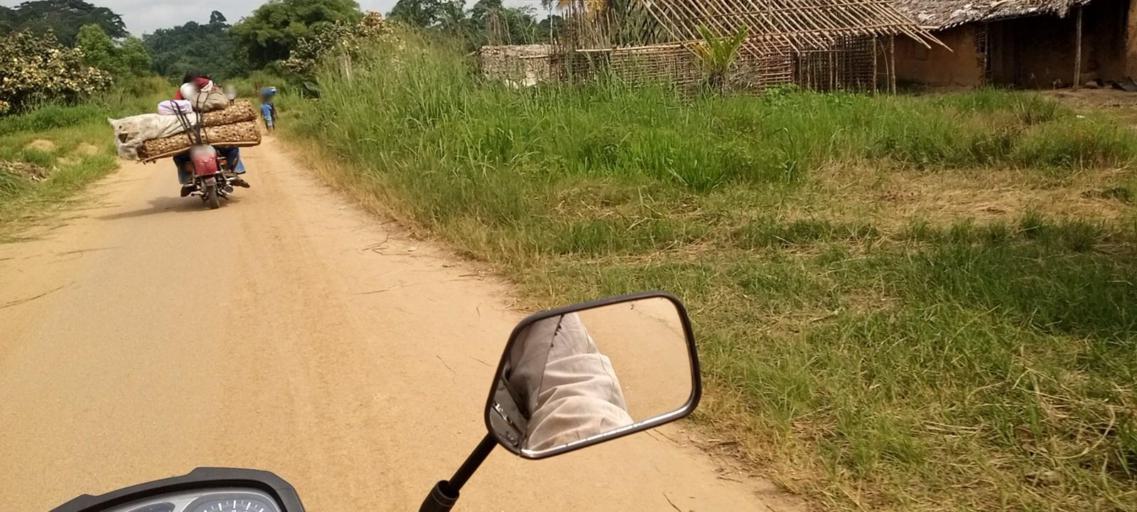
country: CD
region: Eastern Province
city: Kisangani
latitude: 0.3886
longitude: 25.3886
